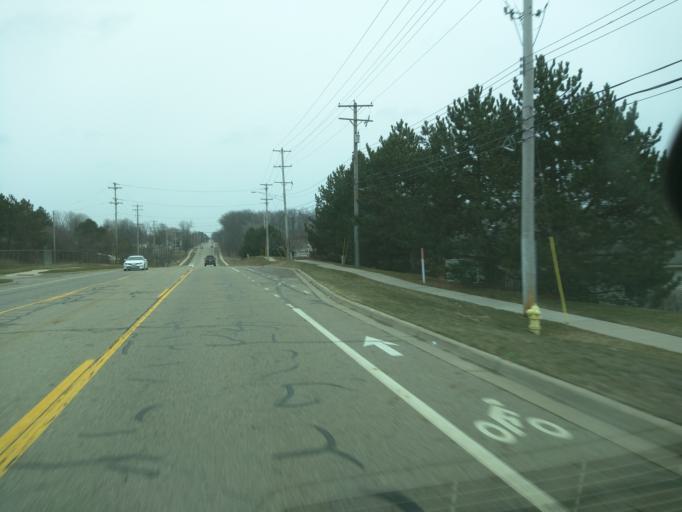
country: US
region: Michigan
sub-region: Eaton County
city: Waverly
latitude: 42.7555
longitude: -84.6567
